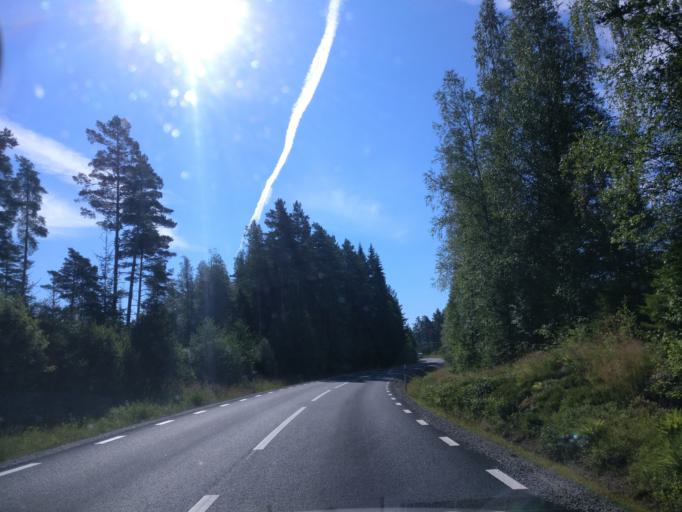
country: SE
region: Vaermland
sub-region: Hagfors Kommun
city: Hagfors
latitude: 60.0386
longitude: 13.8244
